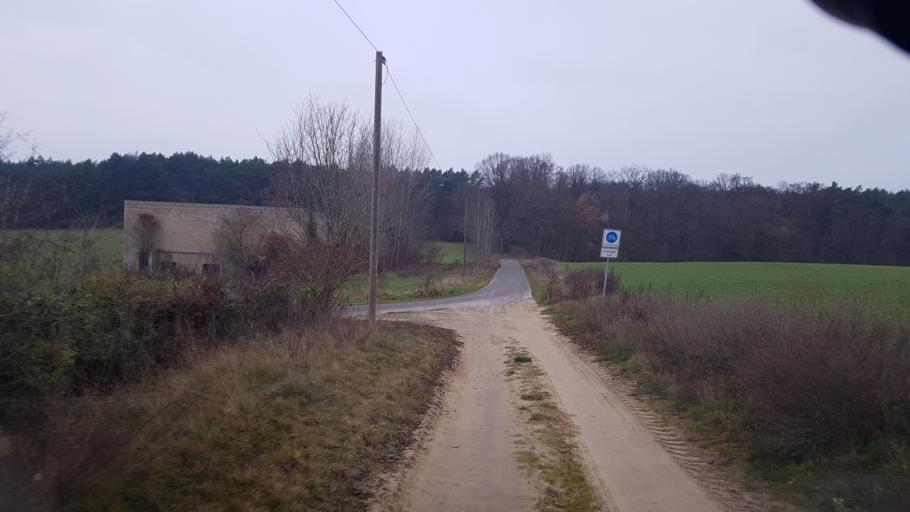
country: DE
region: Brandenburg
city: Schenkendobern
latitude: 51.9666
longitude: 14.6546
